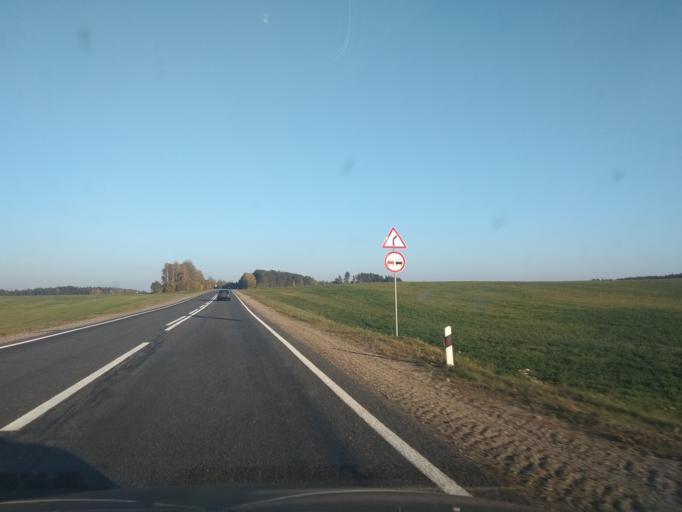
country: BY
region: Grodnenskaya
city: Zel'va
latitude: 53.1405
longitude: 24.6972
